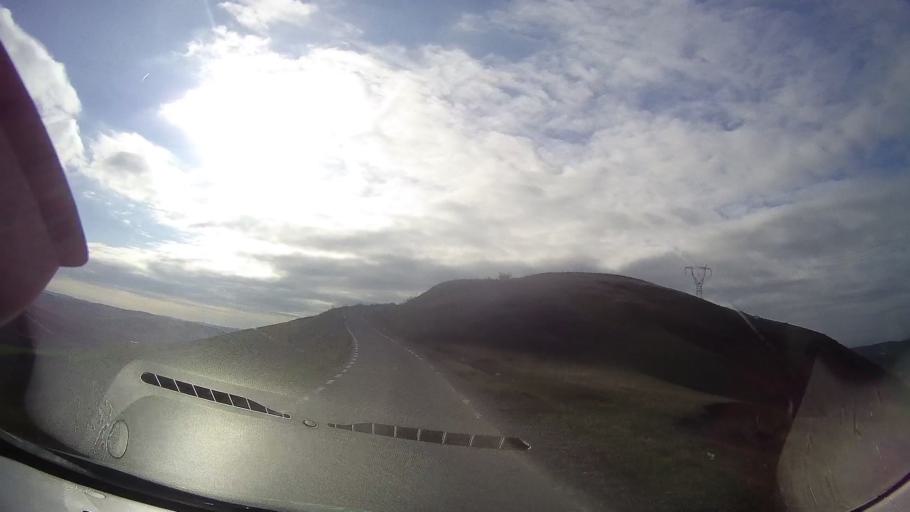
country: RO
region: Mures
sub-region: Comuna Sanger
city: Sanger
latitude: 46.5527
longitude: 24.1608
